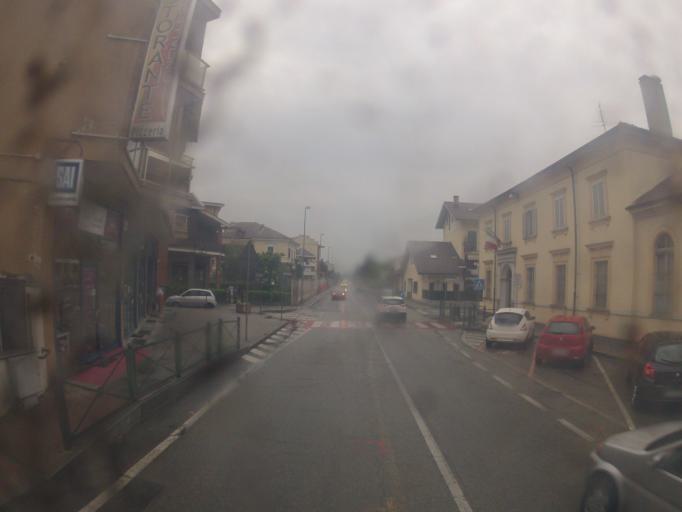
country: IT
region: Piedmont
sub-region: Provincia di Torino
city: La Loggia
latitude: 44.9580
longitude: 7.6672
